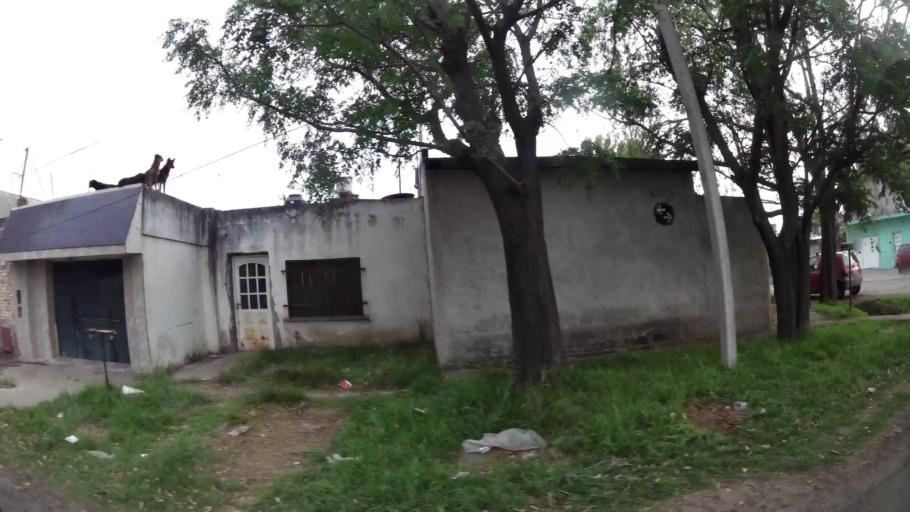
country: AR
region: Santa Fe
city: Gobernador Galvez
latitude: -32.9983
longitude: -60.6863
